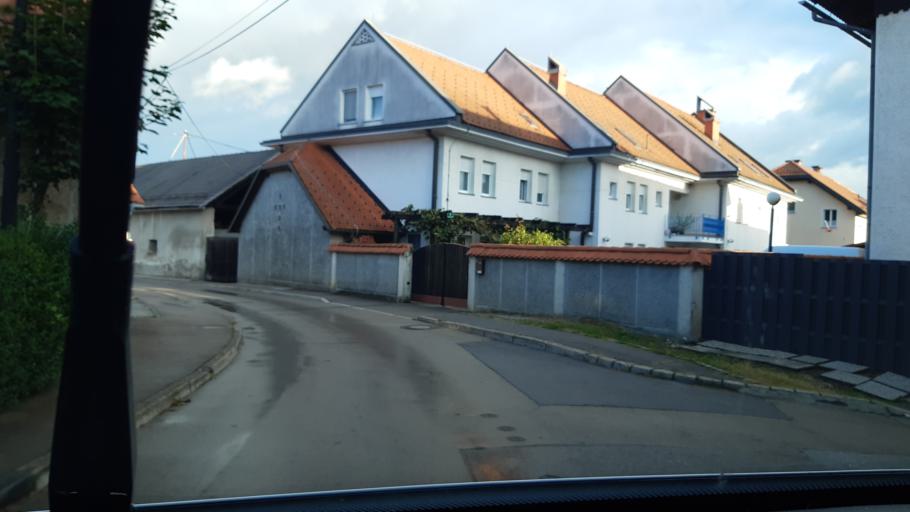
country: SI
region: Ljubljana
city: Ljubljana
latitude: 46.0500
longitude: 14.5416
